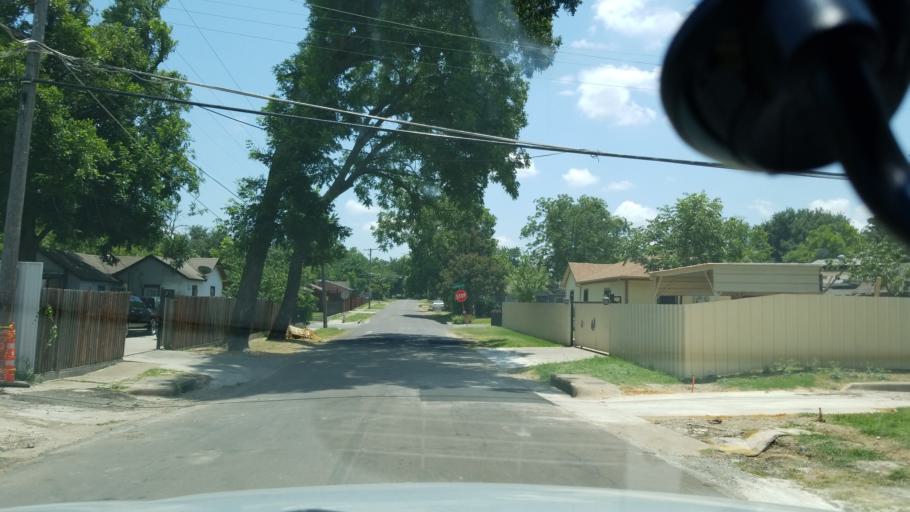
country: US
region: Texas
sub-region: Dallas County
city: Cockrell Hill
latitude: 32.7297
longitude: -96.8662
